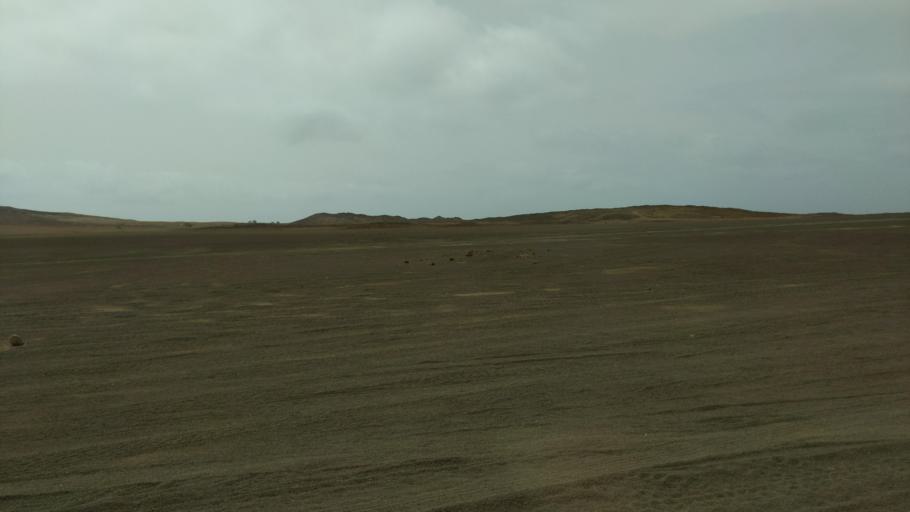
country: CV
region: Sal
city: Espargos
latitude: 16.8004
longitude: -22.9689
